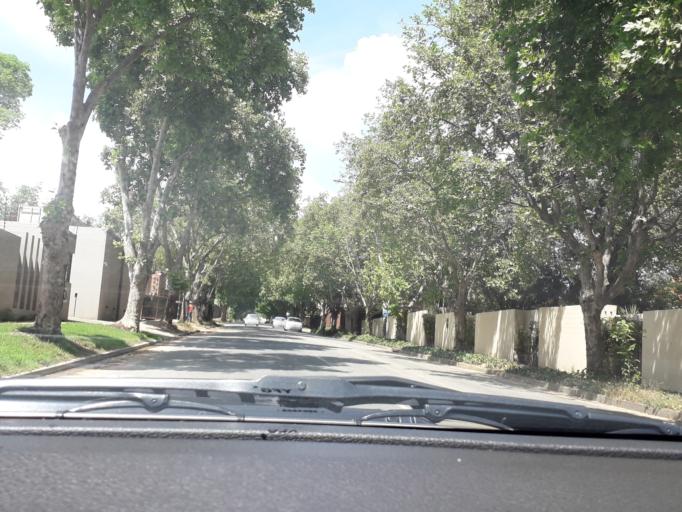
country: ZA
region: Gauteng
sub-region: City of Johannesburg Metropolitan Municipality
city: Johannesburg
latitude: -26.1586
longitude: 28.0585
